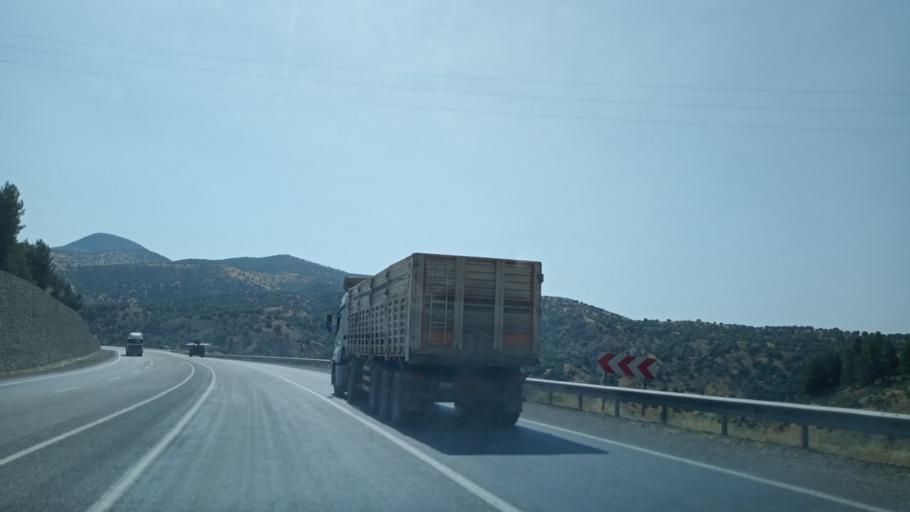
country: TR
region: Siirt
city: Baykan
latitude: 38.1327
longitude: 41.7468
